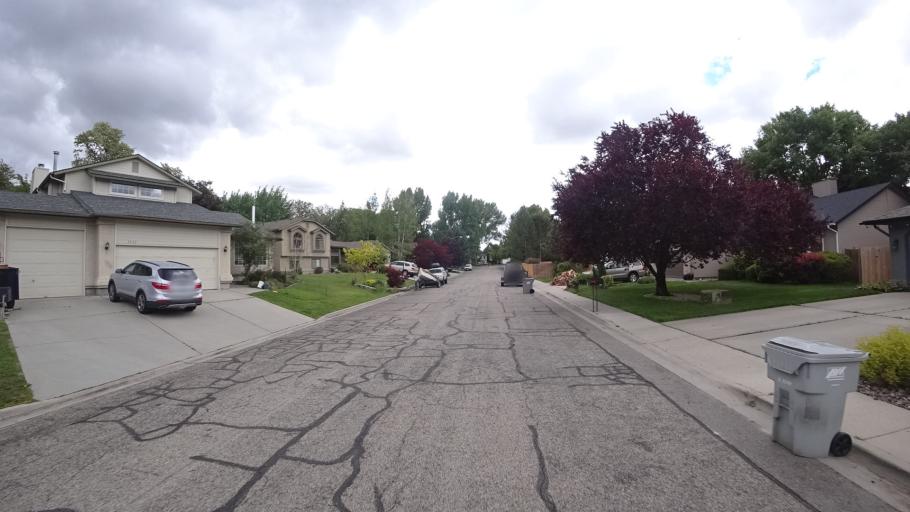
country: US
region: Idaho
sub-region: Ada County
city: Garden City
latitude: 43.6706
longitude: -116.2569
